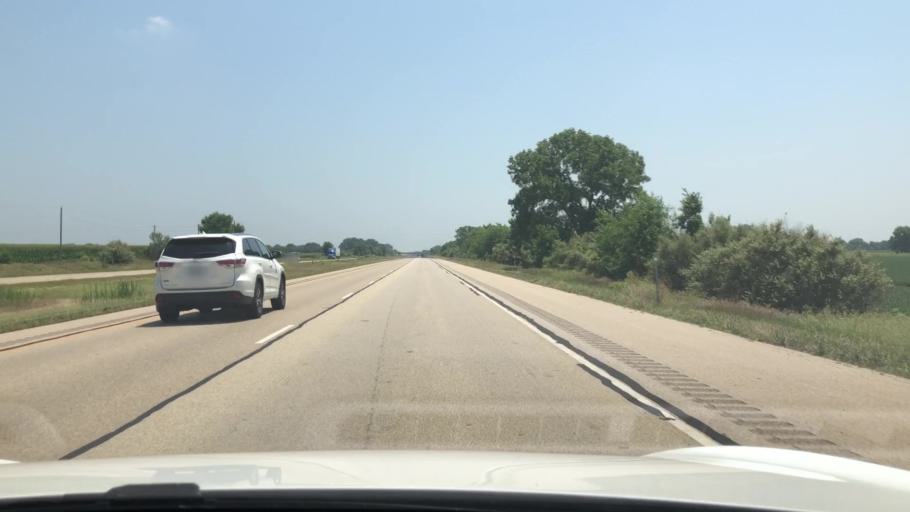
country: US
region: Illinois
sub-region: McLean County
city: Downs
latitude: 40.4082
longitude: -88.9181
